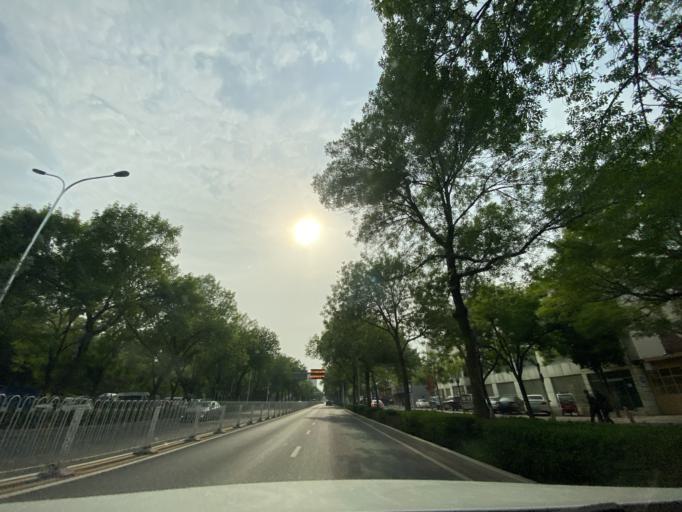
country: CN
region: Beijing
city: Qinghe
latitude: 39.9753
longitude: 116.3570
